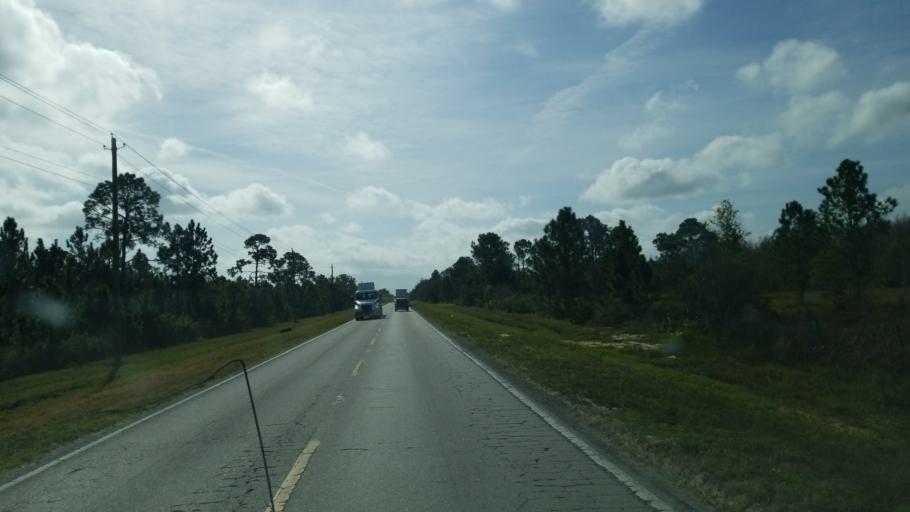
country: US
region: Florida
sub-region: Polk County
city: Polk City
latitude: 28.1935
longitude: -81.7497
